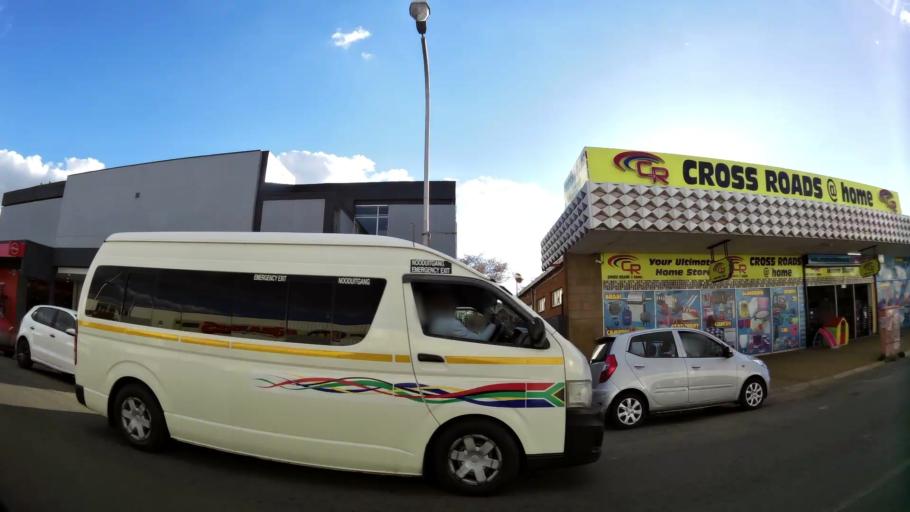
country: ZA
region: North-West
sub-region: Dr Kenneth Kaunda District Municipality
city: Potchefstroom
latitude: -26.7101
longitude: 27.0974
